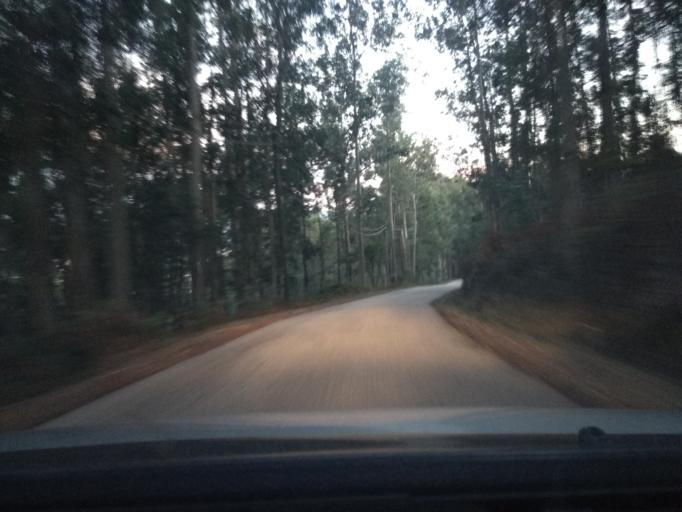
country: ES
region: Galicia
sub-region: Provincia de Pontevedra
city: Moana
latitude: 42.2992
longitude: -8.6954
